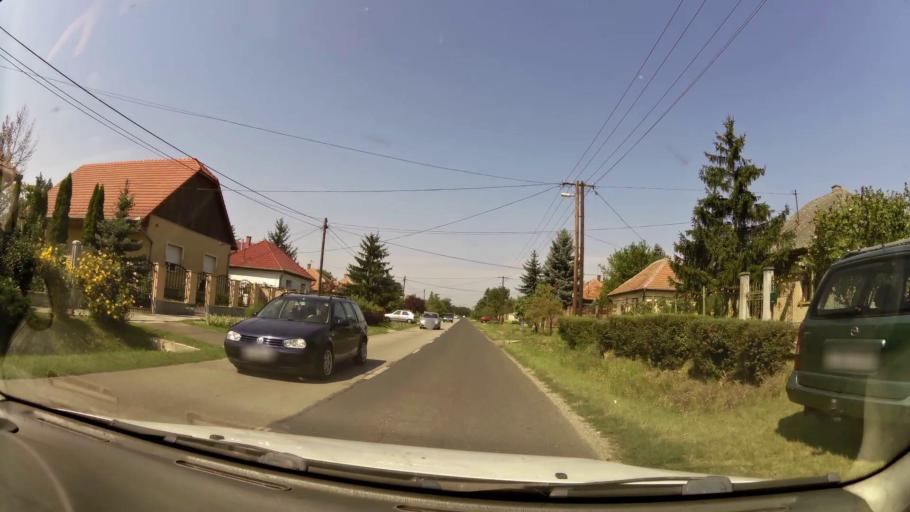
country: HU
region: Pest
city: Tapiosag
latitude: 47.4050
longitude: 19.6215
